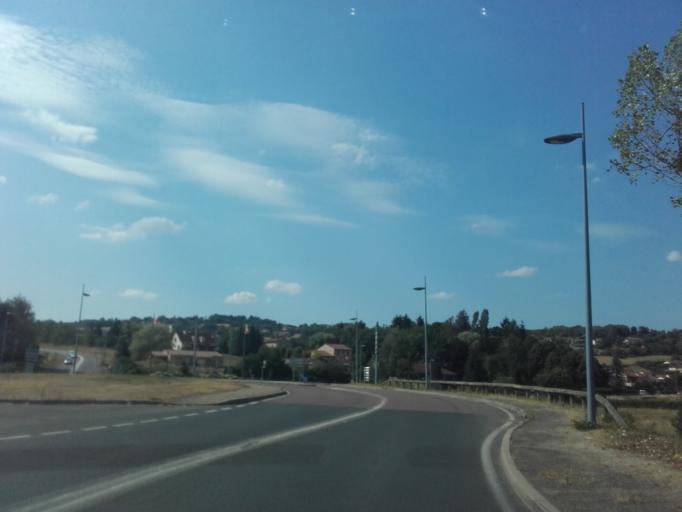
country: FR
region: Bourgogne
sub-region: Departement de Saone-et-Loire
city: Cluny
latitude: 46.4393
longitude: 4.6605
